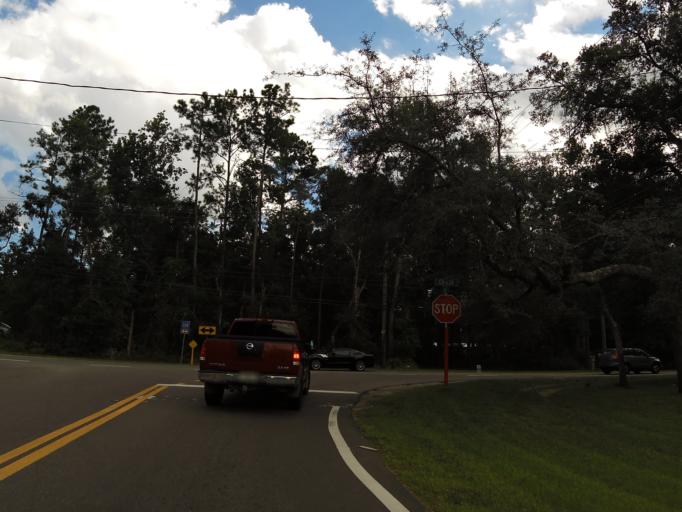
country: US
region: Florida
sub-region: Saint Johns County
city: Saint Augustine
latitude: 29.9065
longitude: -81.4913
